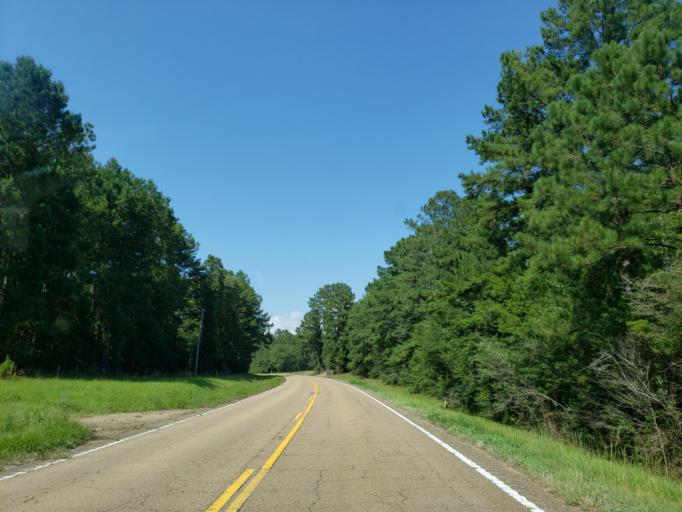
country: US
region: Mississippi
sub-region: Lamar County
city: Sumrall
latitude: 31.4387
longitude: -89.5334
